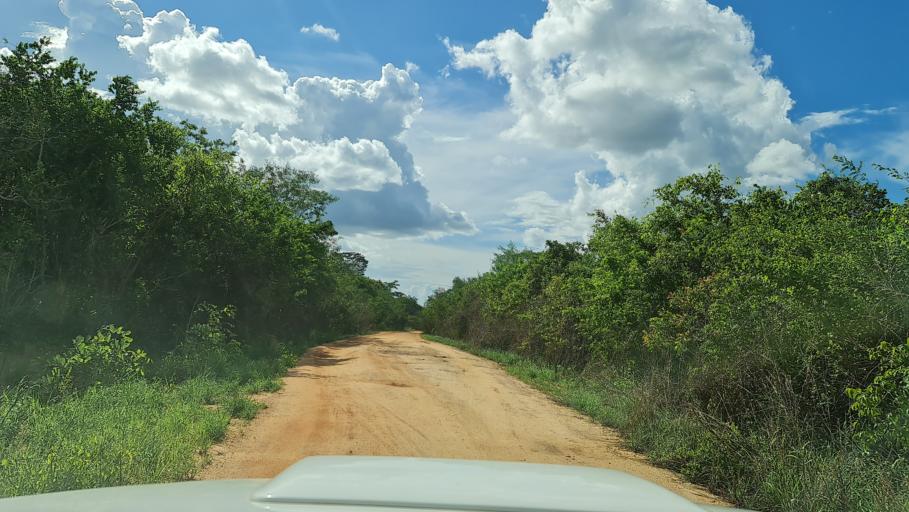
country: MZ
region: Nampula
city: Ilha de Mocambique
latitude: -15.4118
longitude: 40.2514
